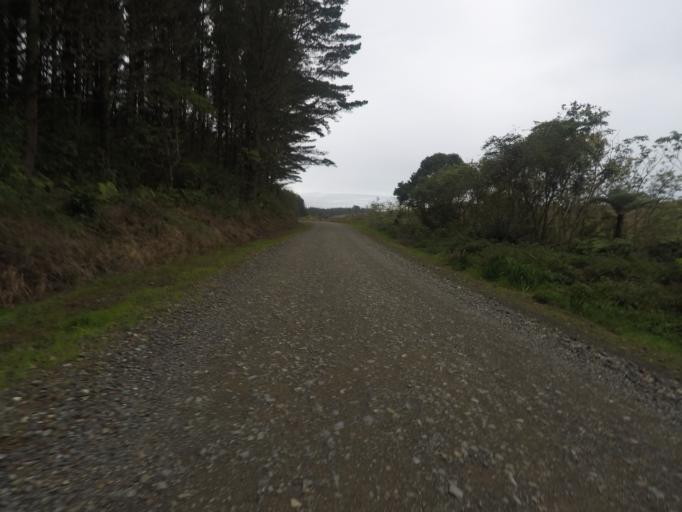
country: NZ
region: Auckland
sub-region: Auckland
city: Muriwai Beach
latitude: -36.7487
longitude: 174.5753
